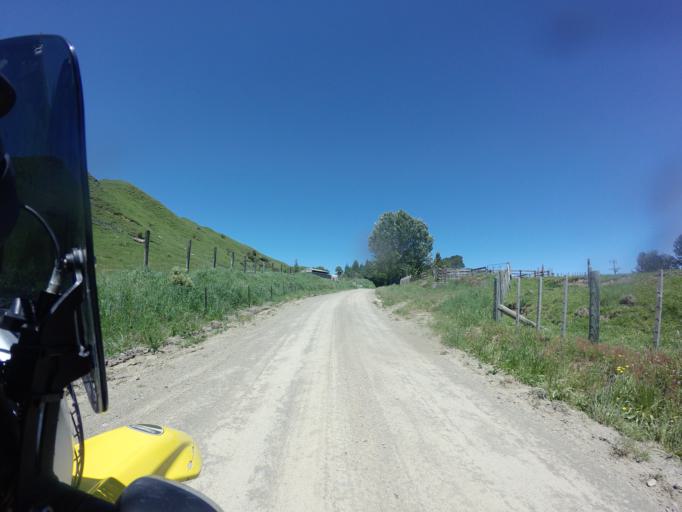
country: NZ
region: Bay of Plenty
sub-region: Opotiki District
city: Opotiki
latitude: -38.3970
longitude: 177.4591
